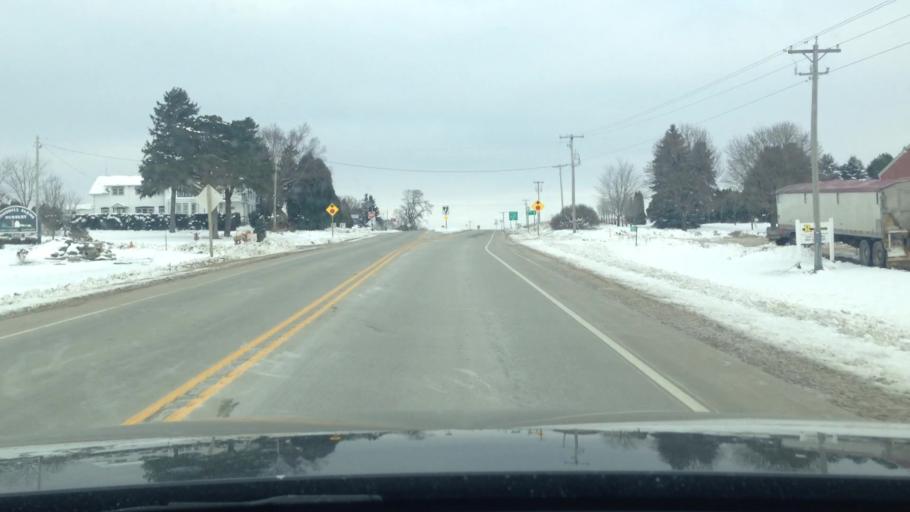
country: US
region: Wisconsin
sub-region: Walworth County
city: Lake Geneva
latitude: 42.5426
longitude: -88.4429
